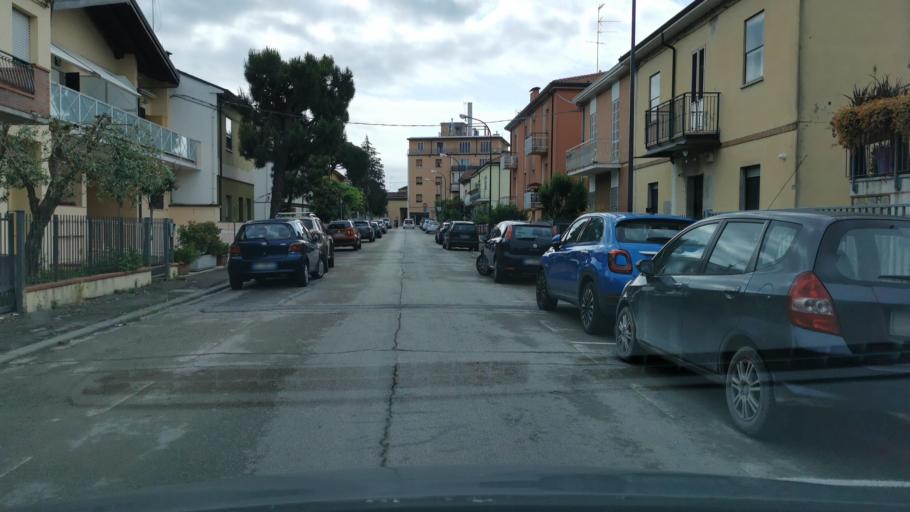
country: IT
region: Emilia-Romagna
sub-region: Provincia di Ravenna
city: Ravenna
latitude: 44.4090
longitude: 12.1983
